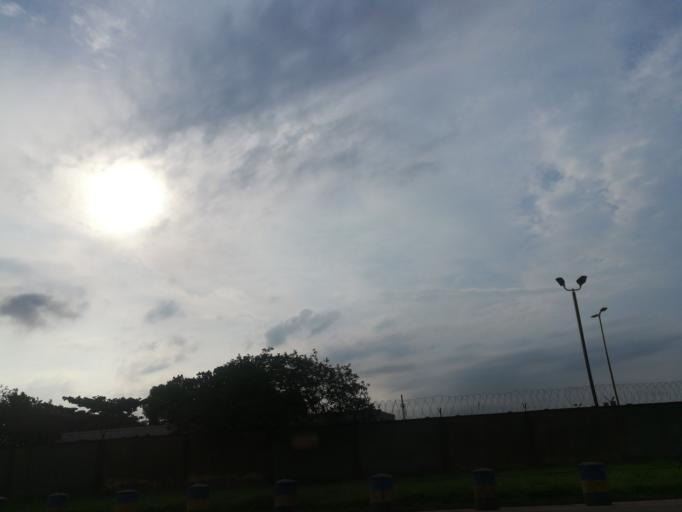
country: NG
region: Rivers
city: Okrika
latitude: 4.7675
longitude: 7.1002
